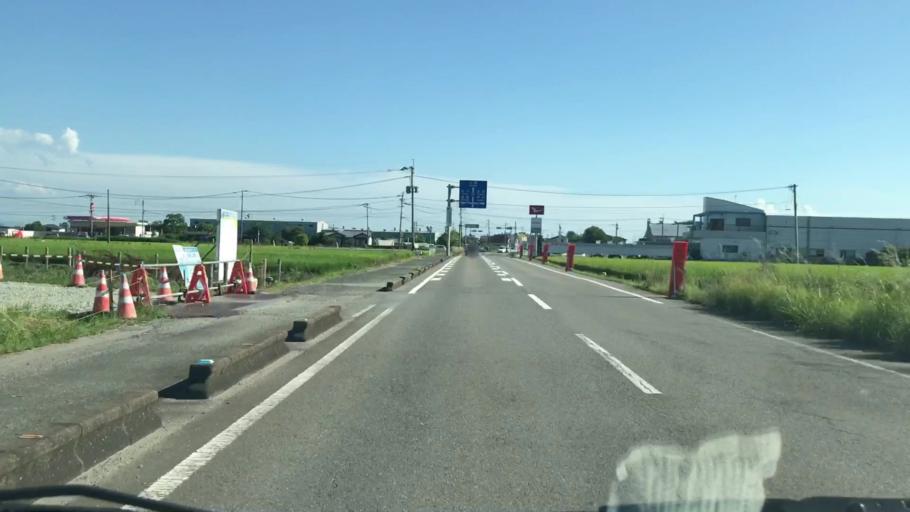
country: JP
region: Saga Prefecture
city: Okawa
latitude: 33.2146
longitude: 130.3352
